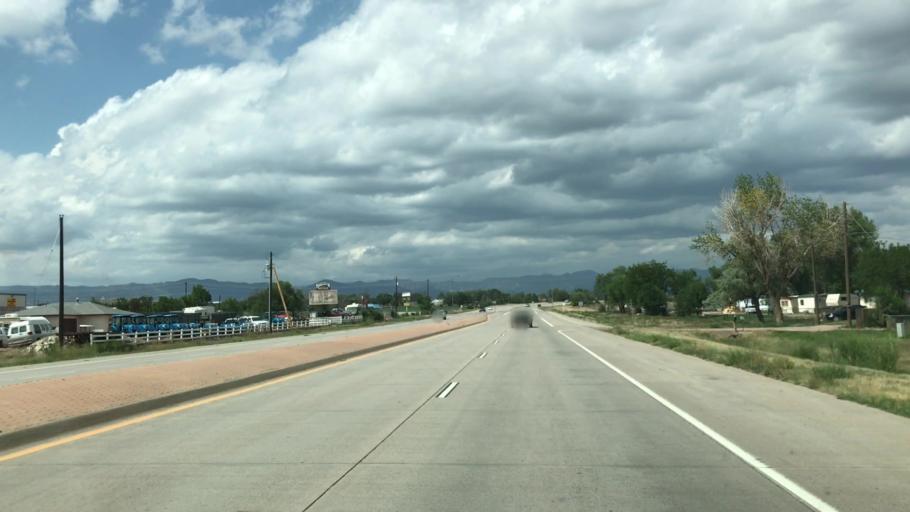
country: US
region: Colorado
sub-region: Fremont County
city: Penrose
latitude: 38.4408
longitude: -105.0239
